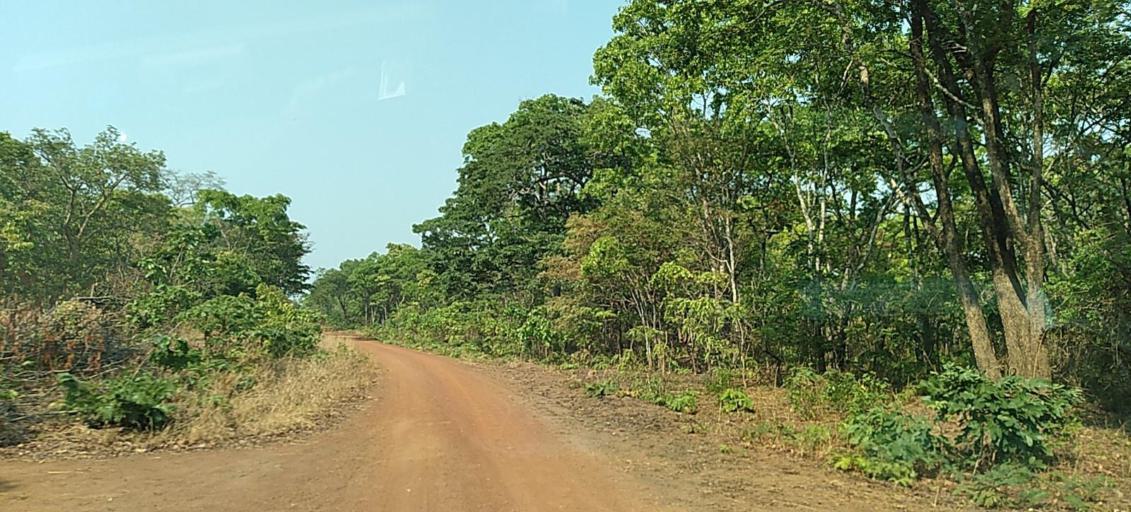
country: ZM
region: Copperbelt
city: Chingola
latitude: -12.8733
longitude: 27.4498
